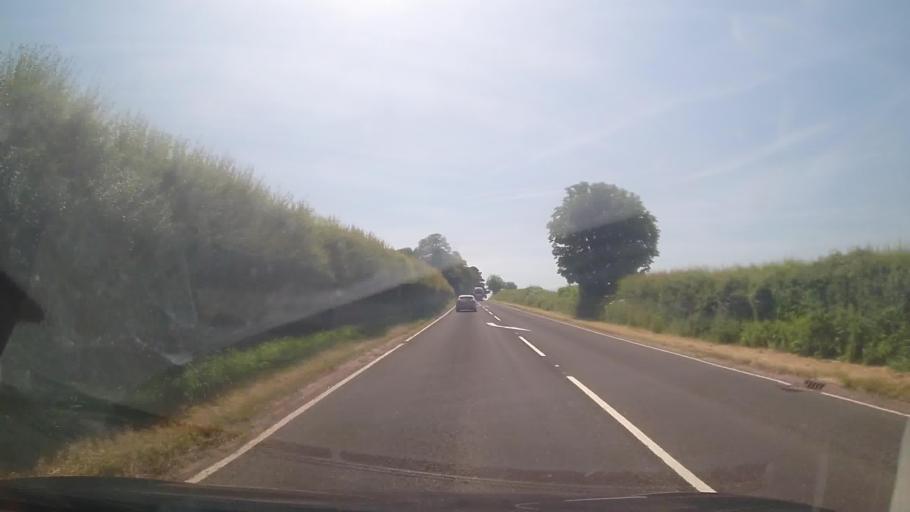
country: GB
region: England
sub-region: Herefordshire
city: Hereford
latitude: 52.0907
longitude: -2.7256
